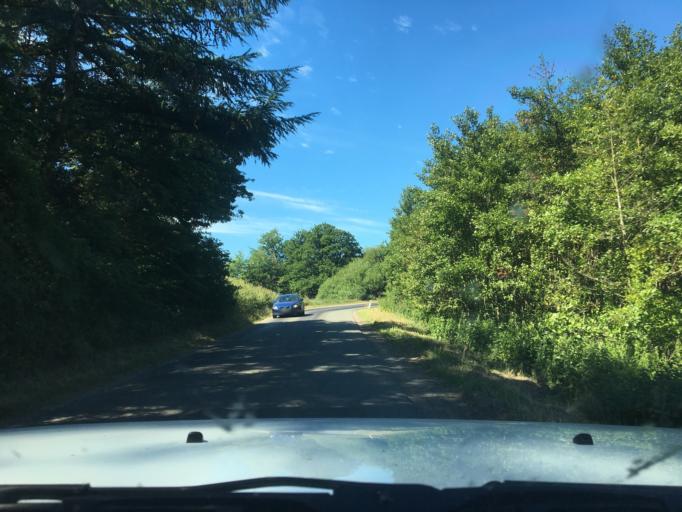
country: DK
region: Central Jutland
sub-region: Syddjurs Kommune
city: Ronde
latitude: 56.3372
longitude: 10.4211
